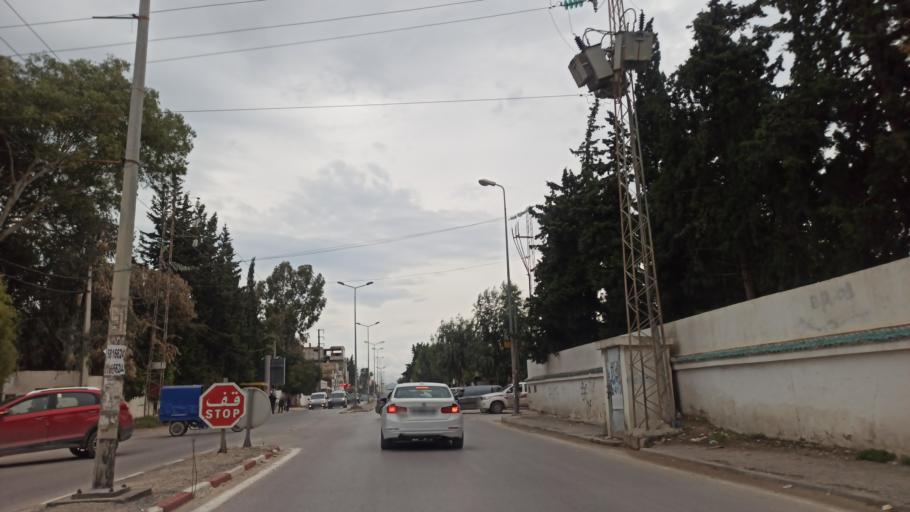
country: TN
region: Ariana
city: Ariana
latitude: 36.8714
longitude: 10.2480
